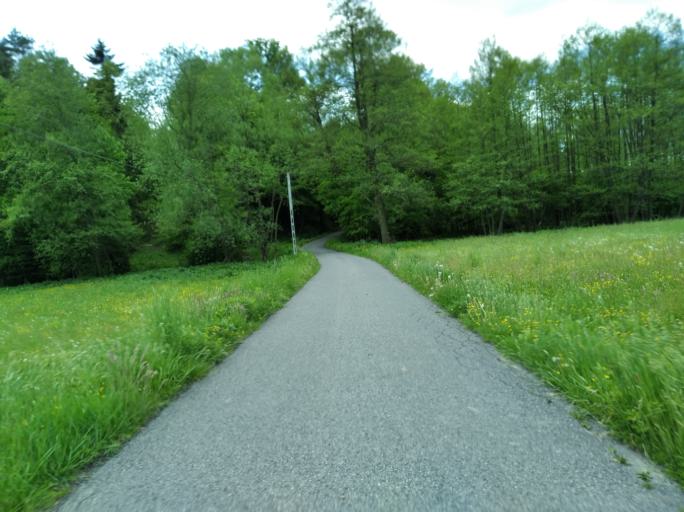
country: PL
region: Subcarpathian Voivodeship
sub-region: Powiat ropczycko-sedziszowski
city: Wielopole Skrzynskie
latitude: 49.9311
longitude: 21.6248
